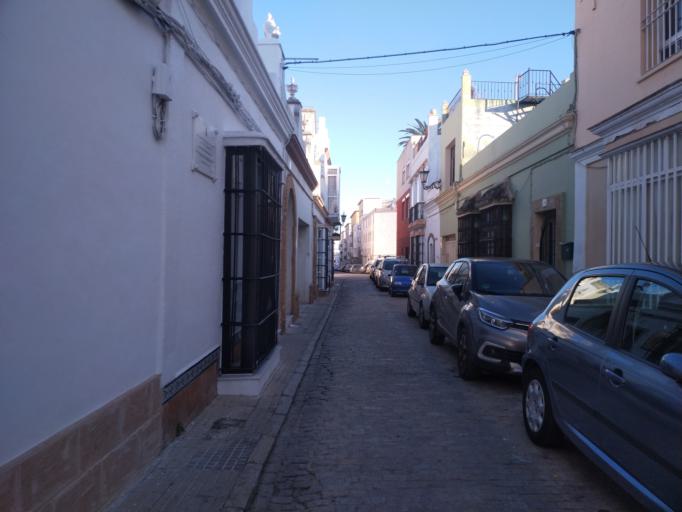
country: ES
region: Andalusia
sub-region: Provincia de Cadiz
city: San Fernando
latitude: 36.4708
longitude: -6.1942
